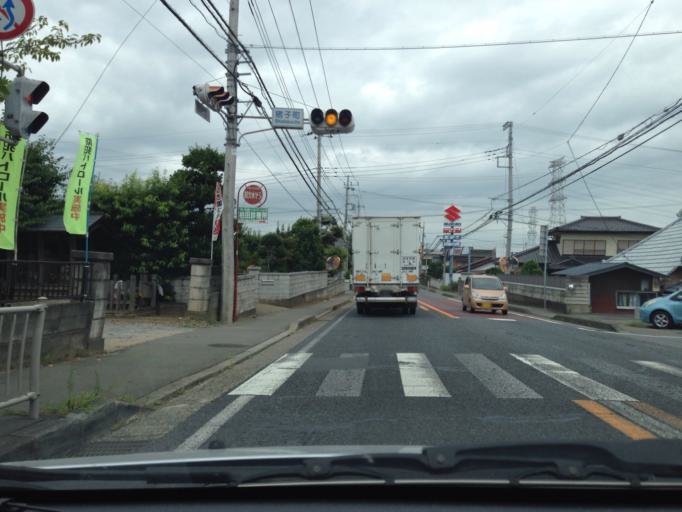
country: JP
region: Ibaraki
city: Ushiku
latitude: 35.9948
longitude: 140.1491
